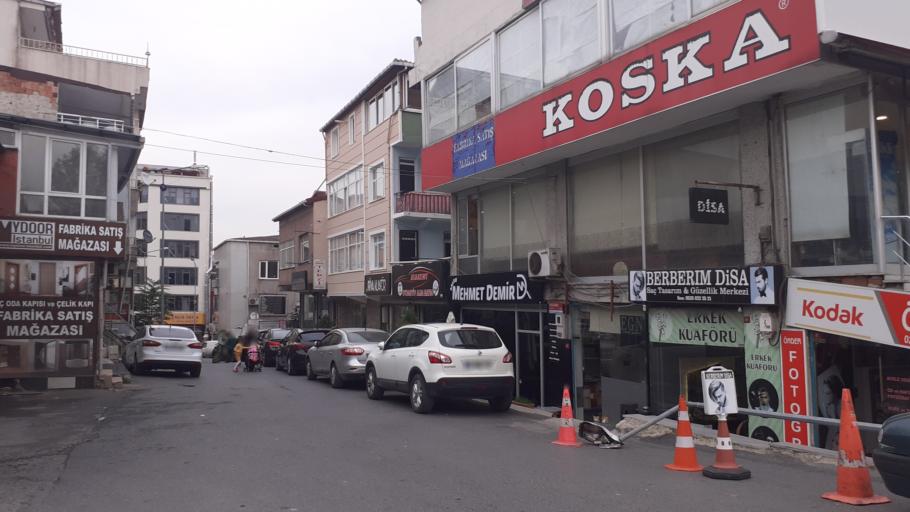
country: TR
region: Istanbul
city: Mahmutbey
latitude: 41.0481
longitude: 28.8000
